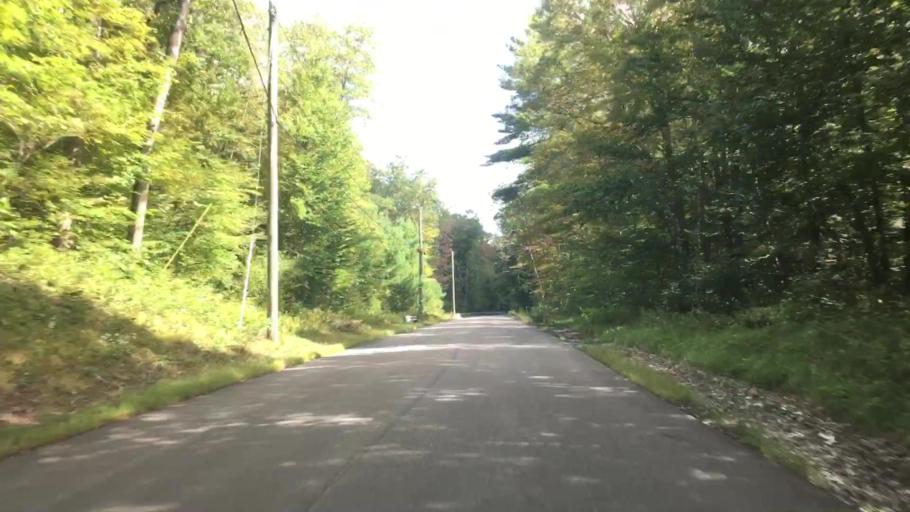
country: US
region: Connecticut
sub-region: Tolland County
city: Stafford Springs
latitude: 41.9247
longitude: -72.2522
